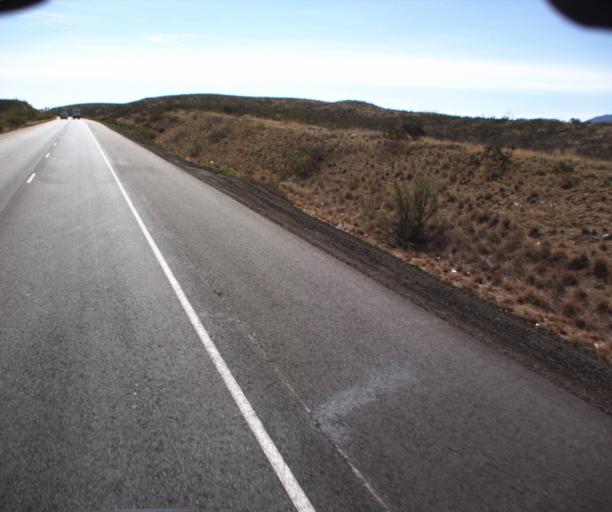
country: US
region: Arizona
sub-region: Cochise County
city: Mescal
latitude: 31.9698
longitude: -110.4815
